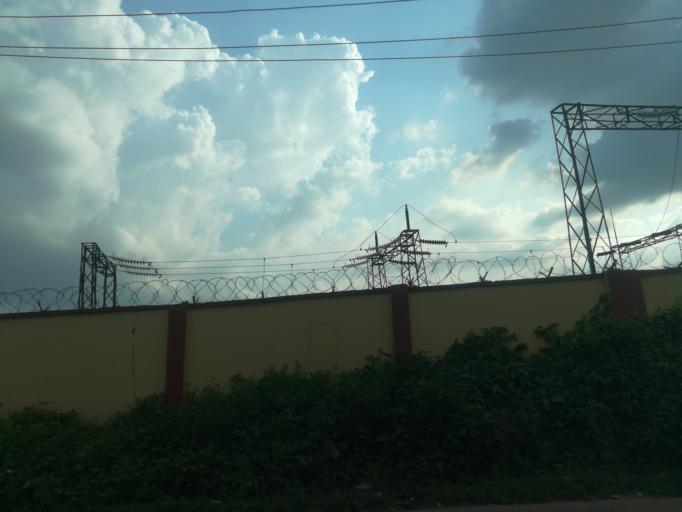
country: NG
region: Oyo
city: Moniya
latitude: 7.4782
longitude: 3.9130
